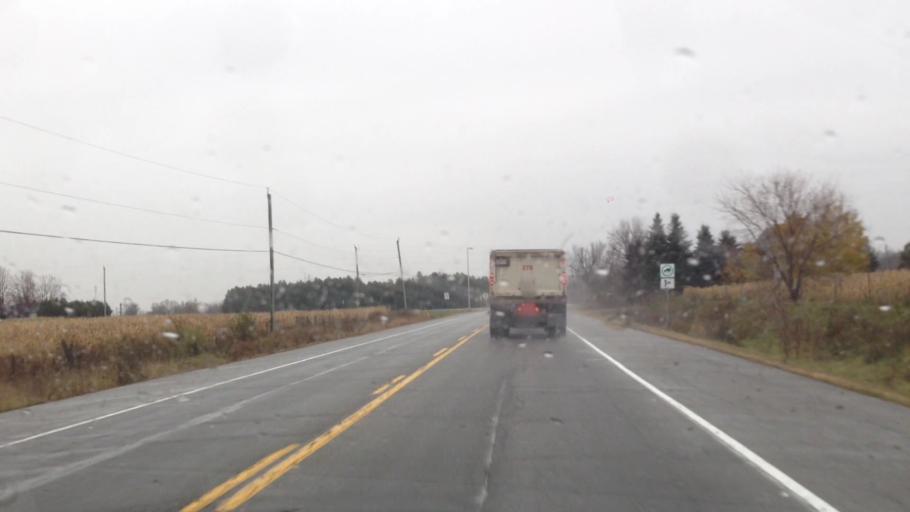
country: CA
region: Ontario
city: Clarence-Rockland
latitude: 45.3474
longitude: -75.3667
